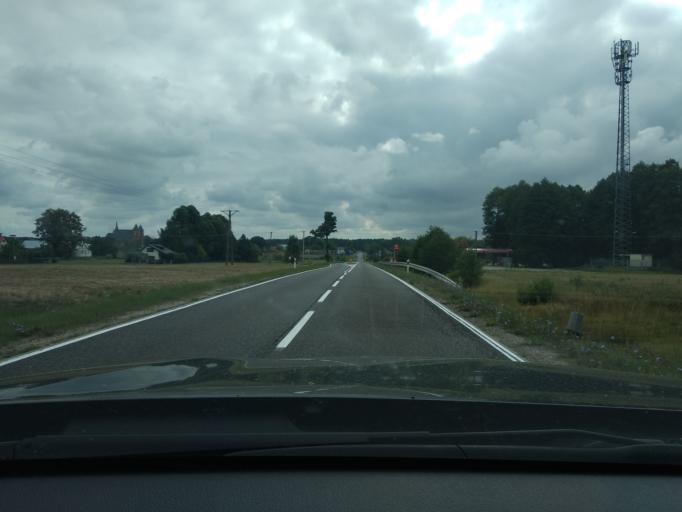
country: PL
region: Masovian Voivodeship
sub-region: Powiat pultuski
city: Obryte
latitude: 52.6509
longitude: 21.2420
